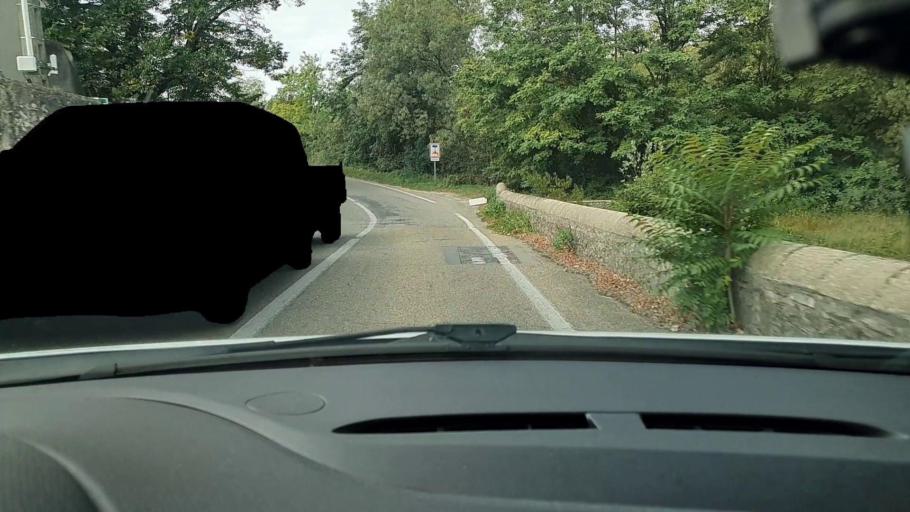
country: FR
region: Languedoc-Roussillon
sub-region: Departement du Gard
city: Saint-Ambroix
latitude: 44.2044
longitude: 4.2487
